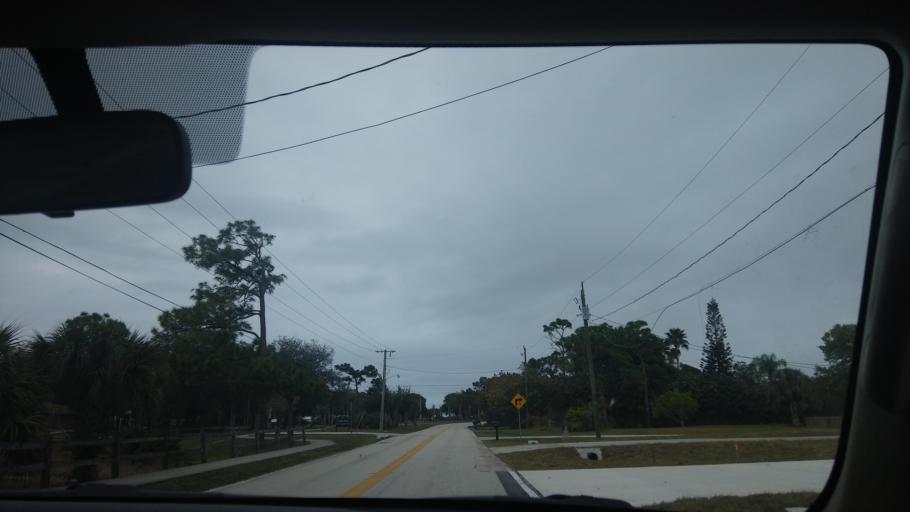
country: US
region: Florida
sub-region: Indian River County
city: Sebastian
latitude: 27.7979
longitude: -80.4947
